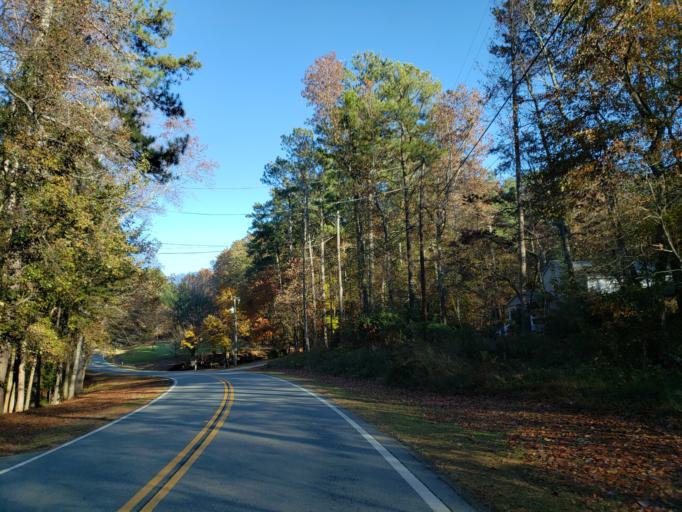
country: US
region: Georgia
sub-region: Cherokee County
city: Woodstock
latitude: 34.0460
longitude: -84.4644
